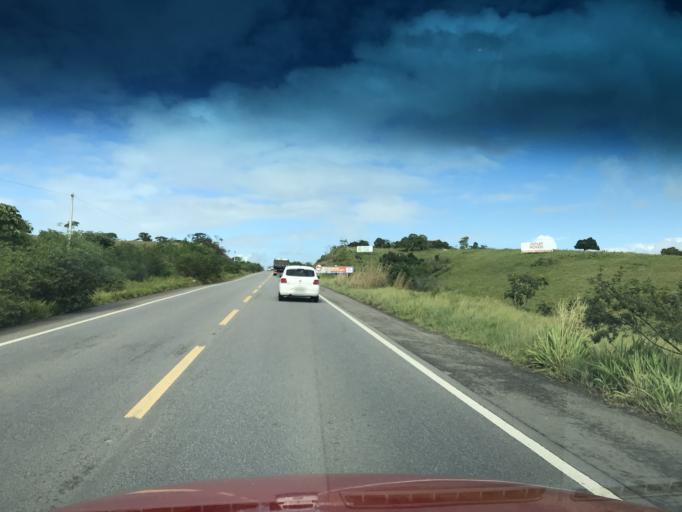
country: BR
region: Bahia
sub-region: Conceicao Do Almeida
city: Muritiba
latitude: -12.9093
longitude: -39.2401
